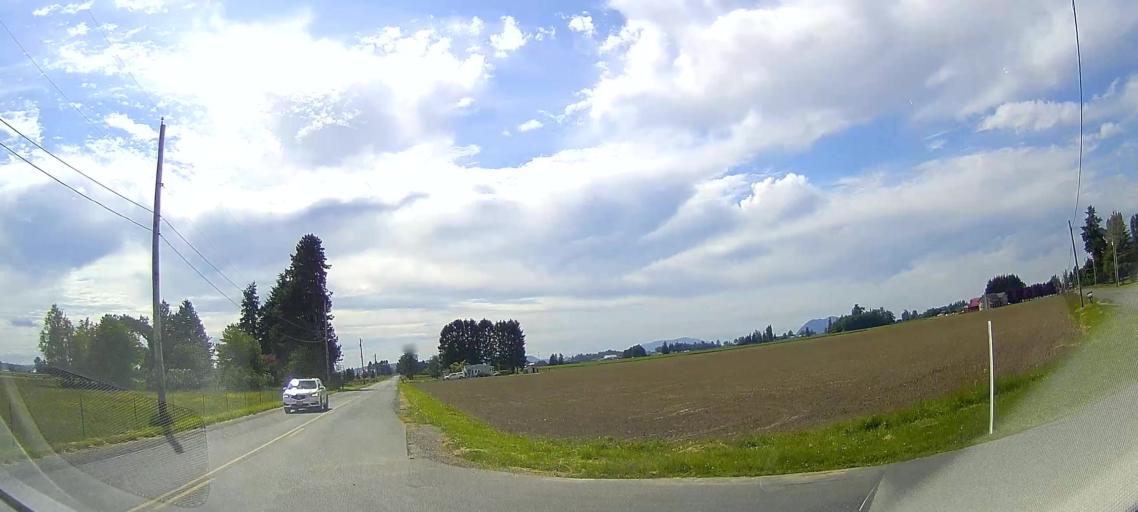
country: US
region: Washington
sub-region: Skagit County
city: Burlington
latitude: 48.5451
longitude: -122.3938
